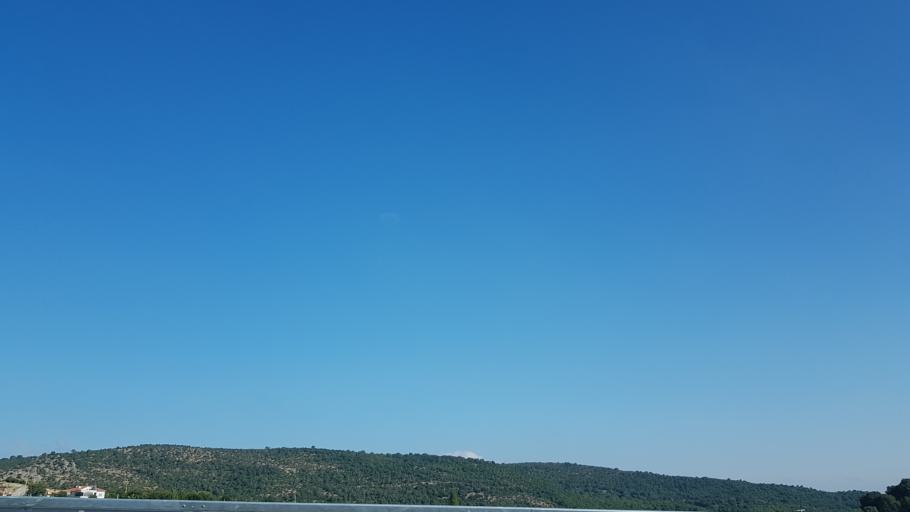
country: TR
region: Balikesir
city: Ertugrul
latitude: 39.5501
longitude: 27.6860
